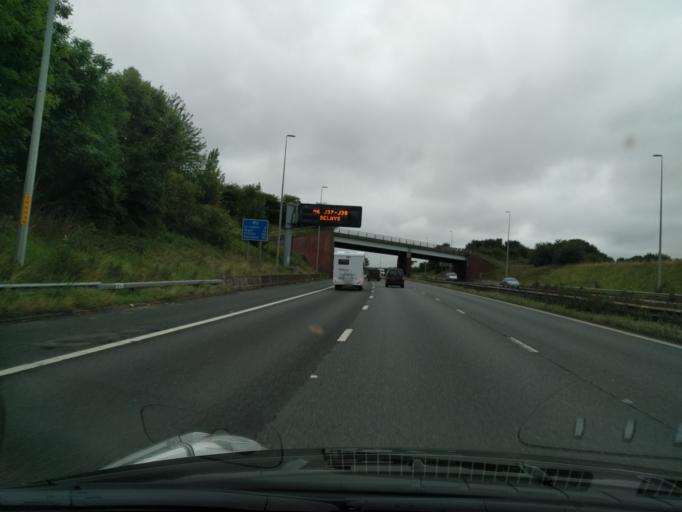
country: GB
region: England
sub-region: St. Helens
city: Newton-le-Willows
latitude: 53.4446
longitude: -2.5891
